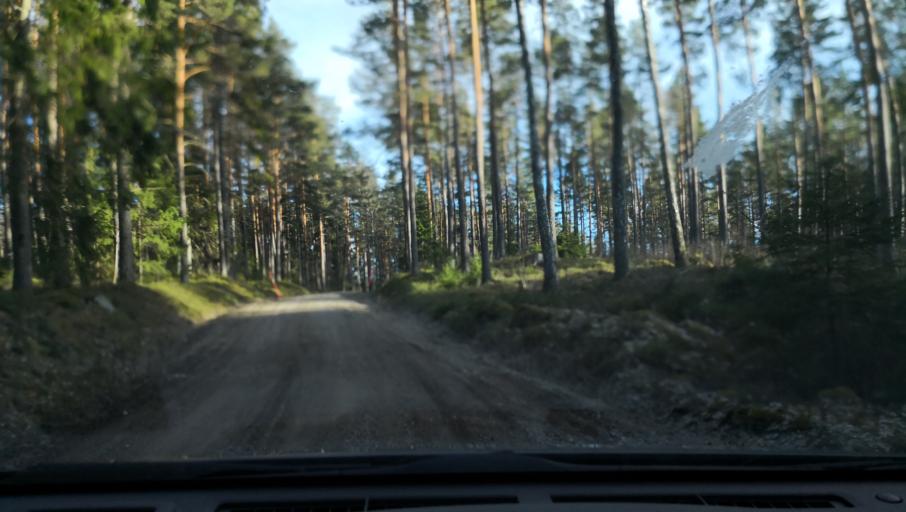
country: SE
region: Vaestmanland
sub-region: Arboga Kommun
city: Arboga
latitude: 59.4354
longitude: 15.7519
